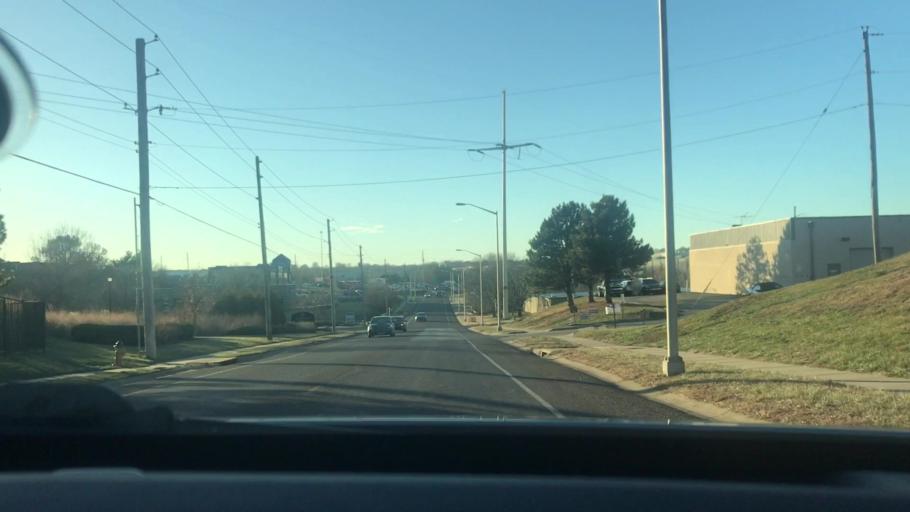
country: US
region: Kansas
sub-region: Johnson County
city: Overland Park
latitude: 38.9858
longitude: -94.7001
